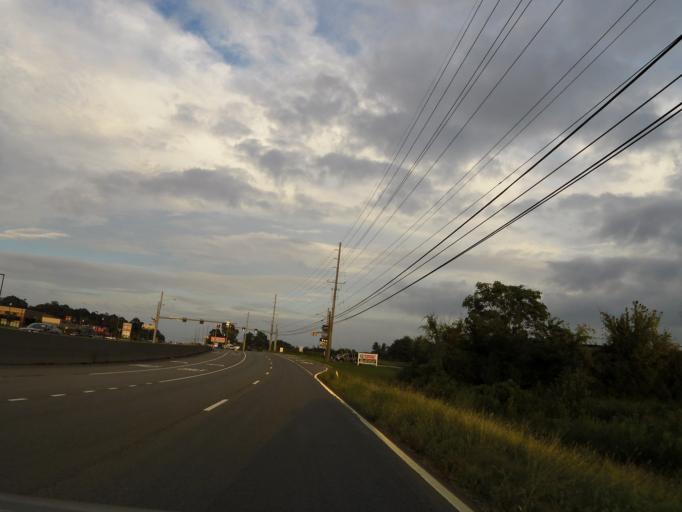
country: US
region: Alabama
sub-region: Madison County
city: Madison
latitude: 34.7472
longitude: -86.7770
